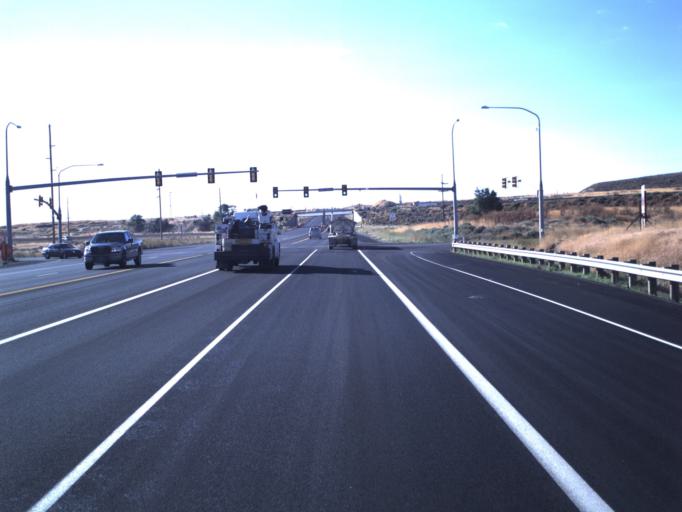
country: US
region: Utah
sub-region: Salt Lake County
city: Oquirrh
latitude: 40.6547
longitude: -112.0769
